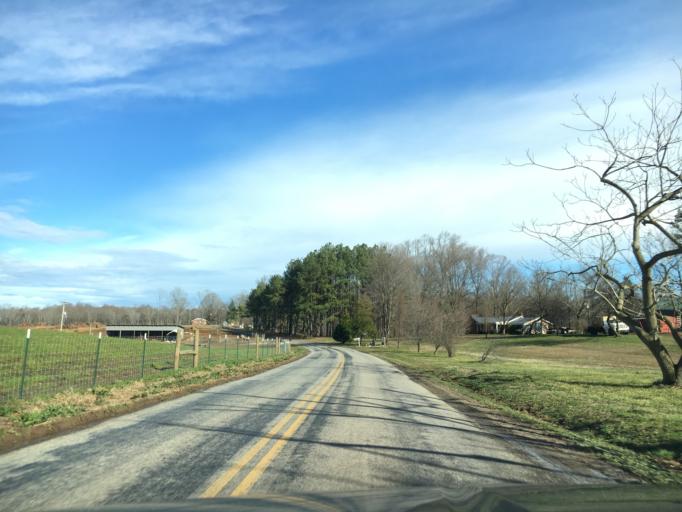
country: US
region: Virginia
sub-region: Amelia County
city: Amelia Court House
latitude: 37.3826
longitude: -78.1256
